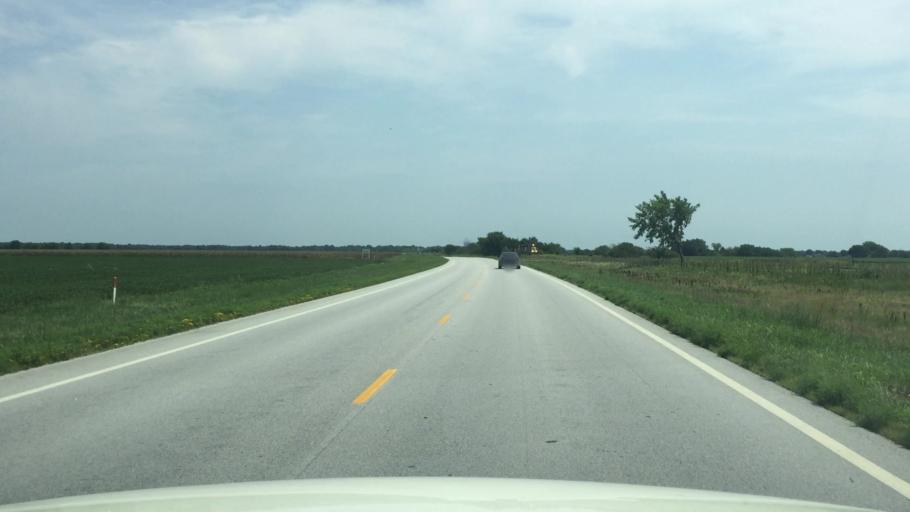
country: US
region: Kansas
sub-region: Labette County
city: Oswego
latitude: 37.1664
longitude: -95.0342
